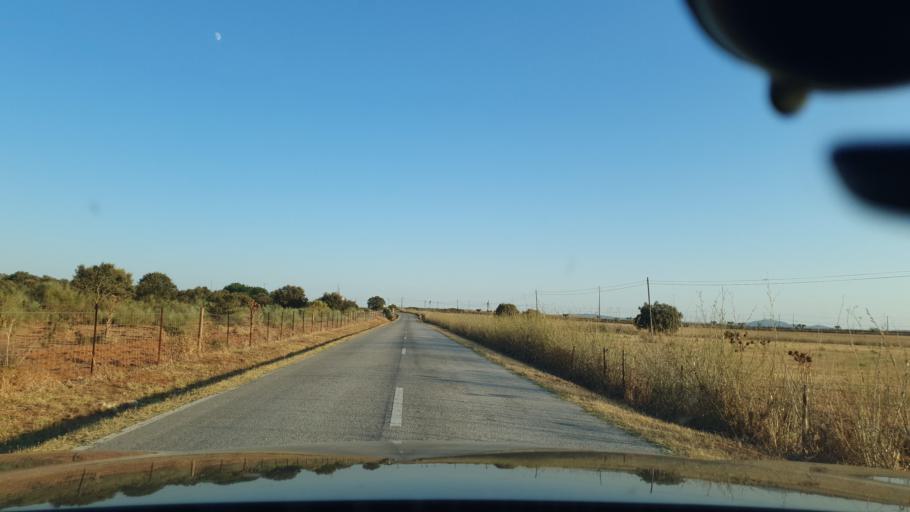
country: PT
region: Evora
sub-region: Estremoz
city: Estremoz
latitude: 38.8998
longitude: -7.6673
